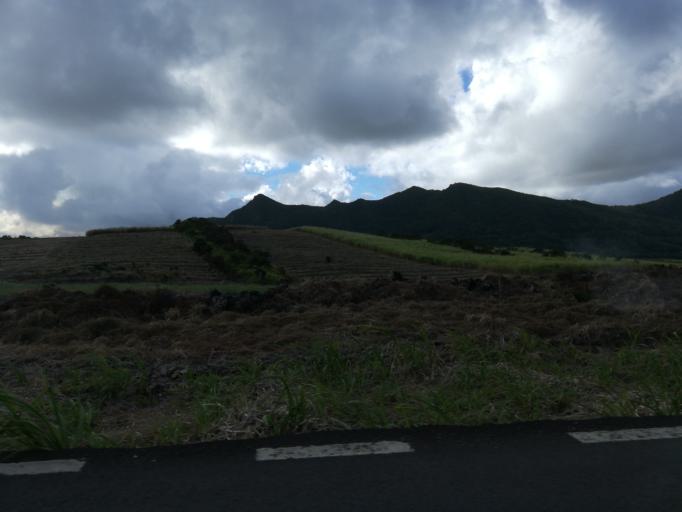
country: MU
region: Flacq
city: Clemencia
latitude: -20.2607
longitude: 57.6985
